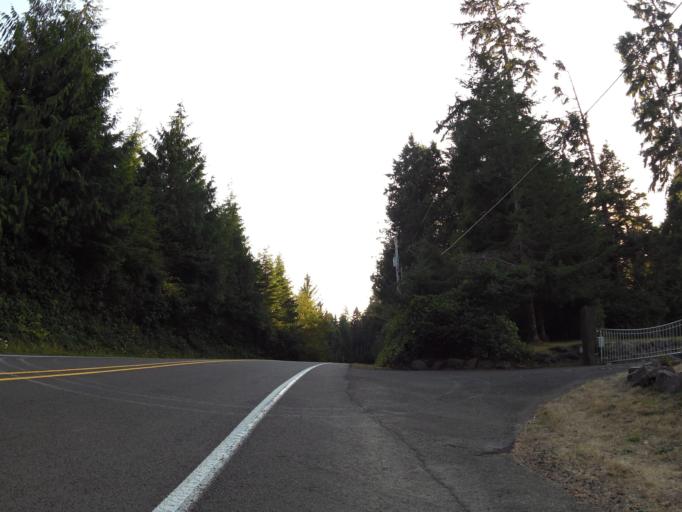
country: US
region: Oregon
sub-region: Lincoln County
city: Lincoln City
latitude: 44.9682
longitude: -123.9915
